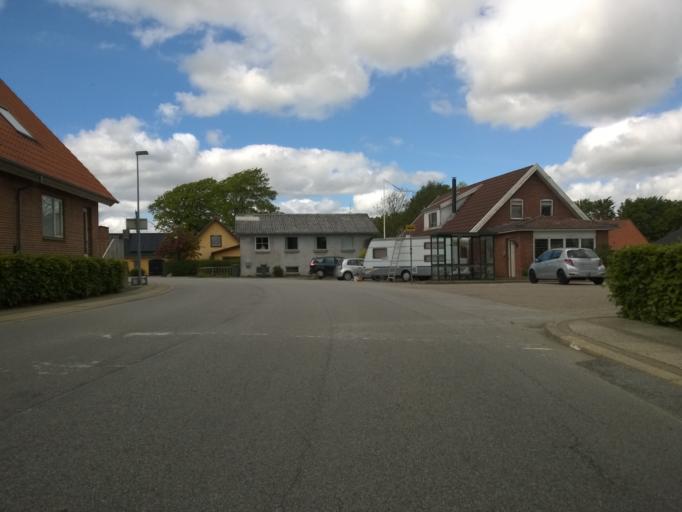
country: DK
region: Central Jutland
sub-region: Holstebro Kommune
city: Vinderup
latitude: 56.4053
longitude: 8.7543
